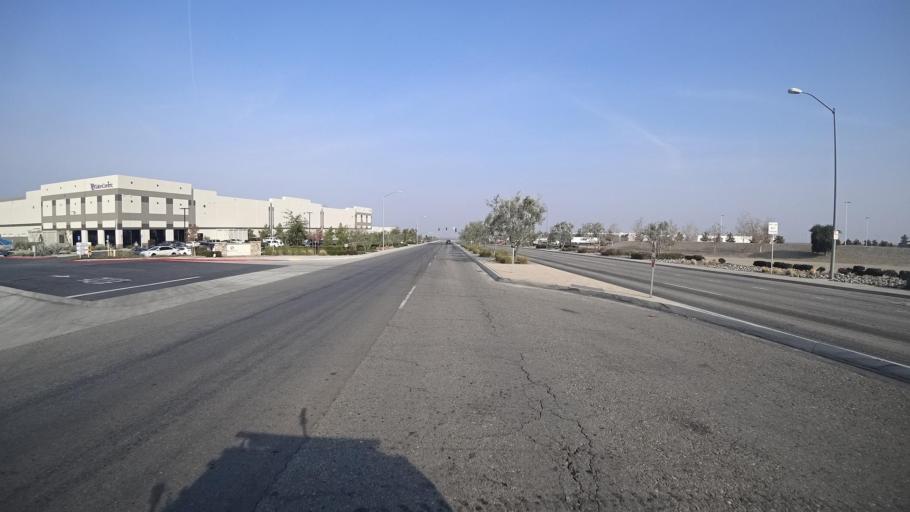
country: US
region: California
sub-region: Kern County
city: Lebec
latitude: 34.9938
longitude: -118.9426
